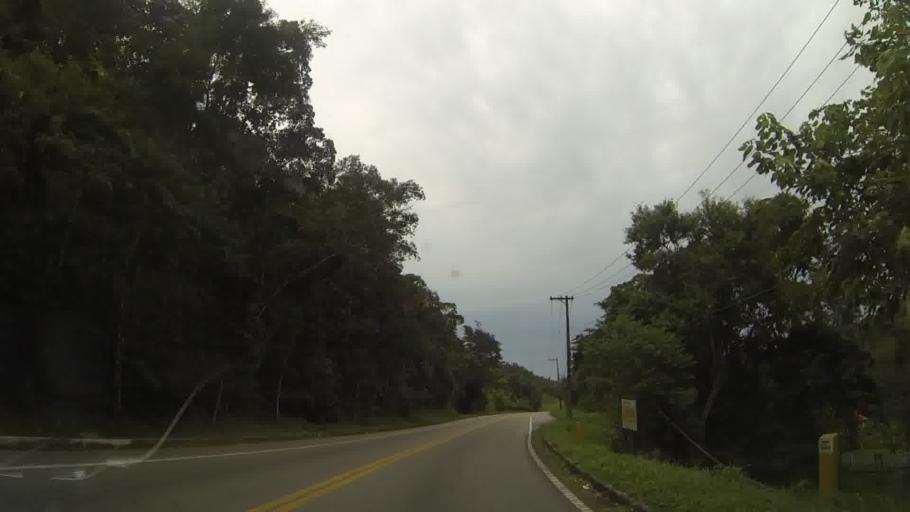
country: BR
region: Sao Paulo
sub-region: Sao Sebastiao
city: Sao Sebastiao
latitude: -23.8146
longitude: -45.4642
